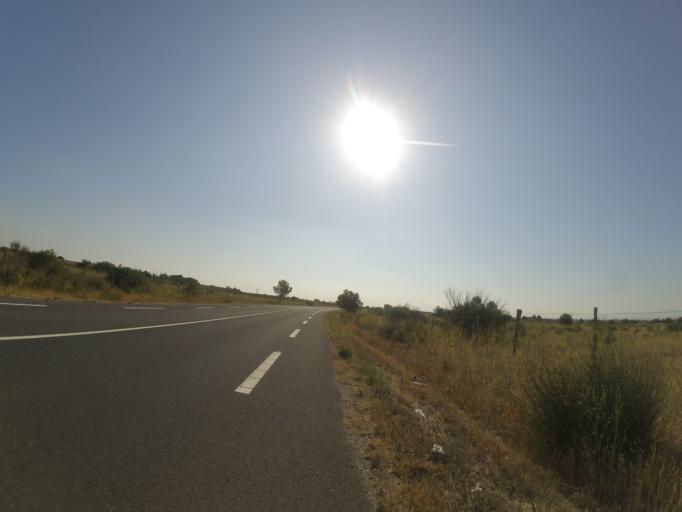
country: FR
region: Languedoc-Roussillon
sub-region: Departement des Pyrenees-Orientales
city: Rivesaltes
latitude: 42.7978
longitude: 2.8645
